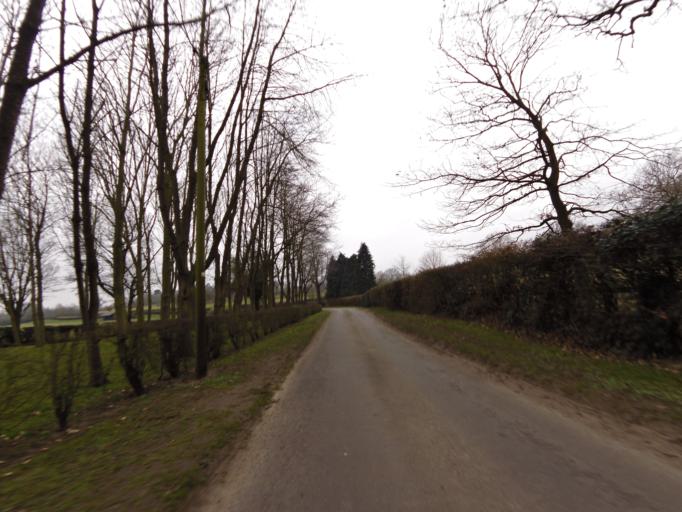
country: GB
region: England
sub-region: Suffolk
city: Framlingham
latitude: 52.2303
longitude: 1.3437
